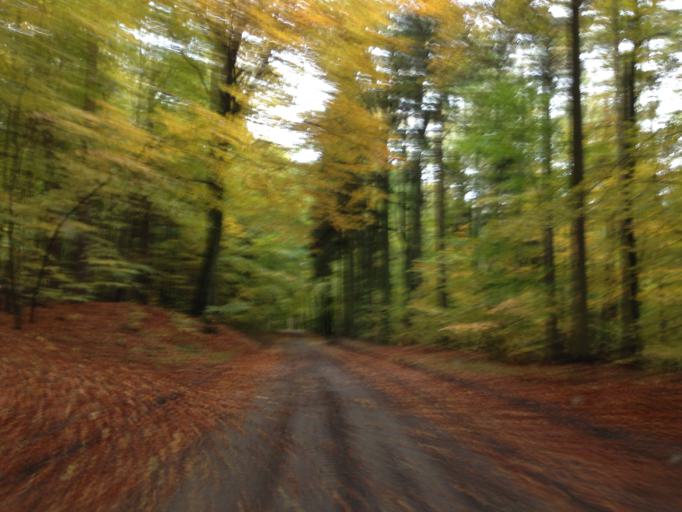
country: PL
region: Warmian-Masurian Voivodeship
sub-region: Powiat ilawski
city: Susz
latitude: 53.6733
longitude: 19.3084
